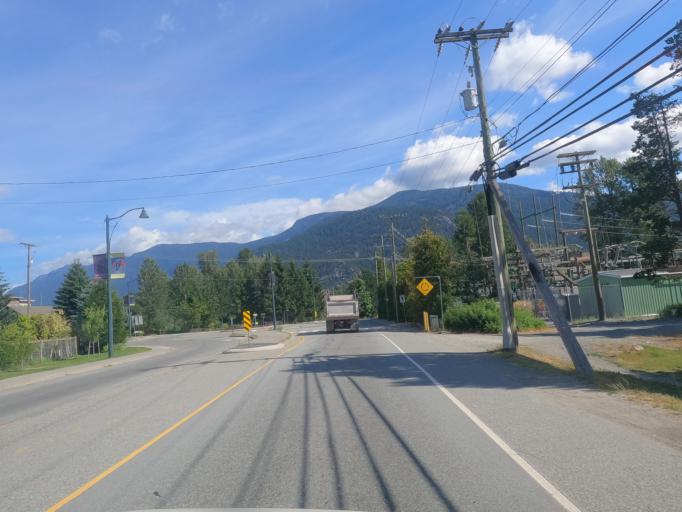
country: CA
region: British Columbia
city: Pemberton
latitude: 50.3214
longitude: -122.8051
